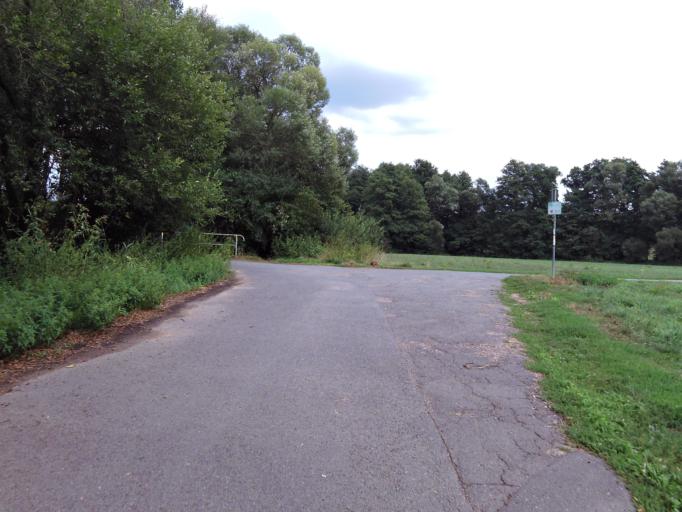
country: DE
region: Hesse
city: Hochst im Odenwald
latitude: 49.7906
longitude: 8.9802
